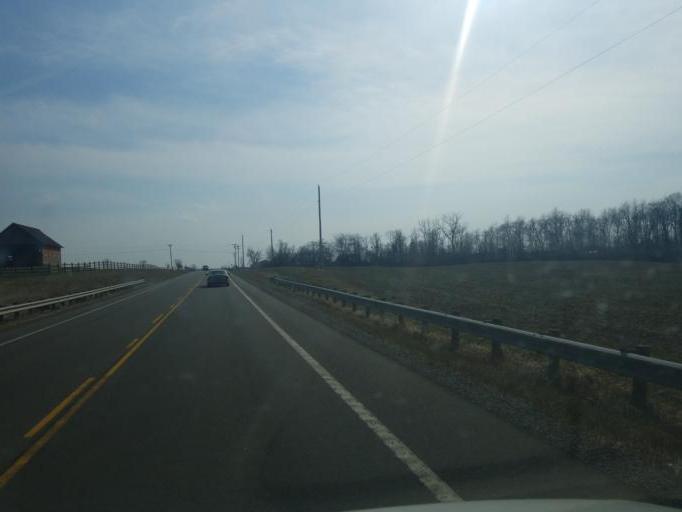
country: US
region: Ohio
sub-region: Logan County
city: Northwood
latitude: 40.4669
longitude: -83.7145
